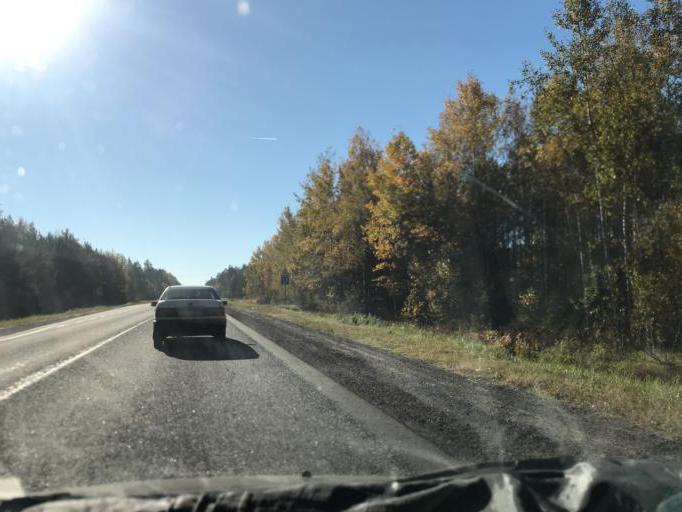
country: BY
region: Mogilev
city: Babruysk
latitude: 53.1681
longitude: 29.0448
